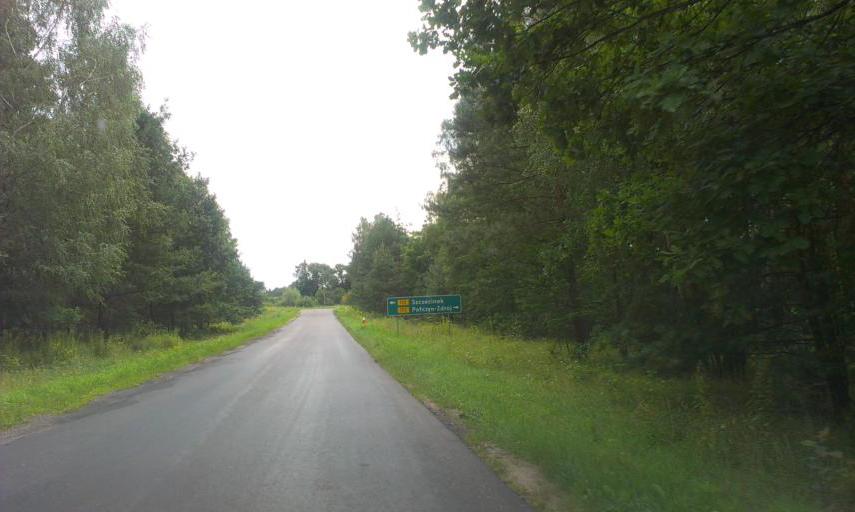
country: PL
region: West Pomeranian Voivodeship
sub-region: Powiat swidwinski
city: Polczyn-Zdroj
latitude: 53.7726
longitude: 16.1511
